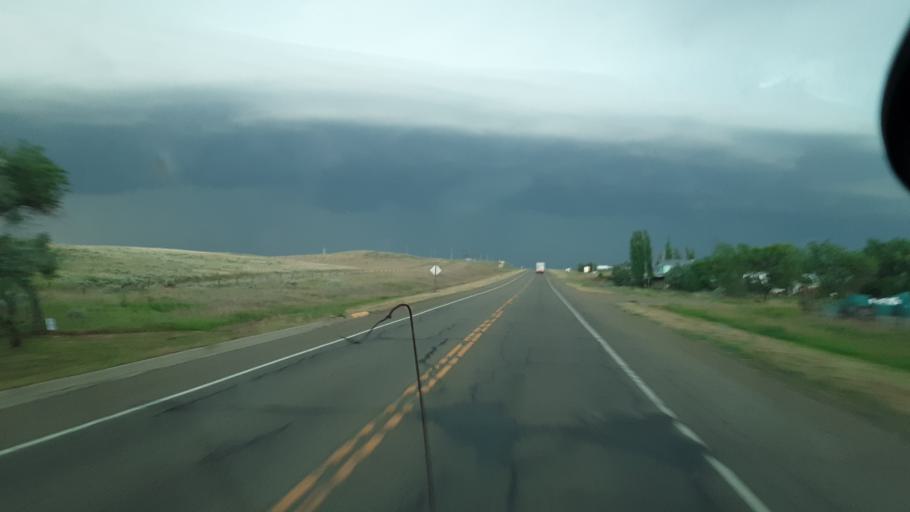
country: US
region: Montana
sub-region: Powder River County
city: Broadus
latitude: 45.4457
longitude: -105.4258
